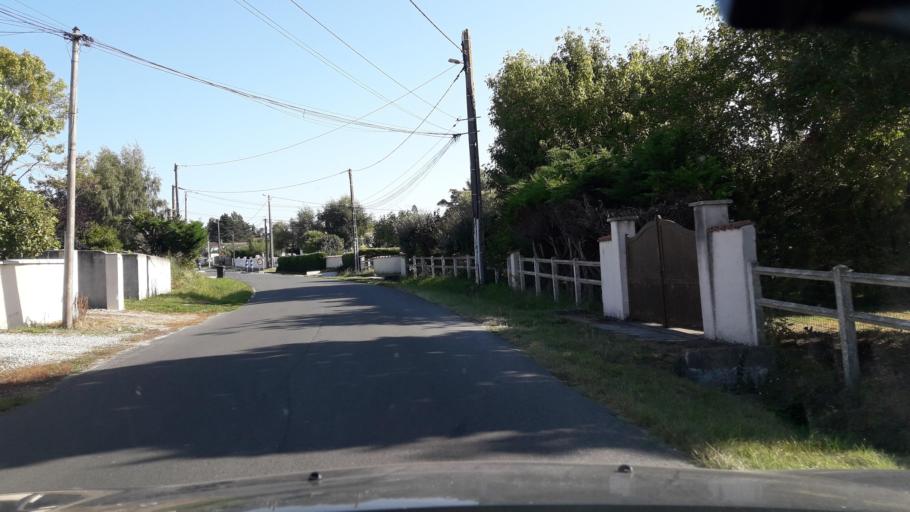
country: FR
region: Poitou-Charentes
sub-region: Departement de la Charente-Maritime
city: Etaules
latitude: 45.7135
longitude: -1.1100
